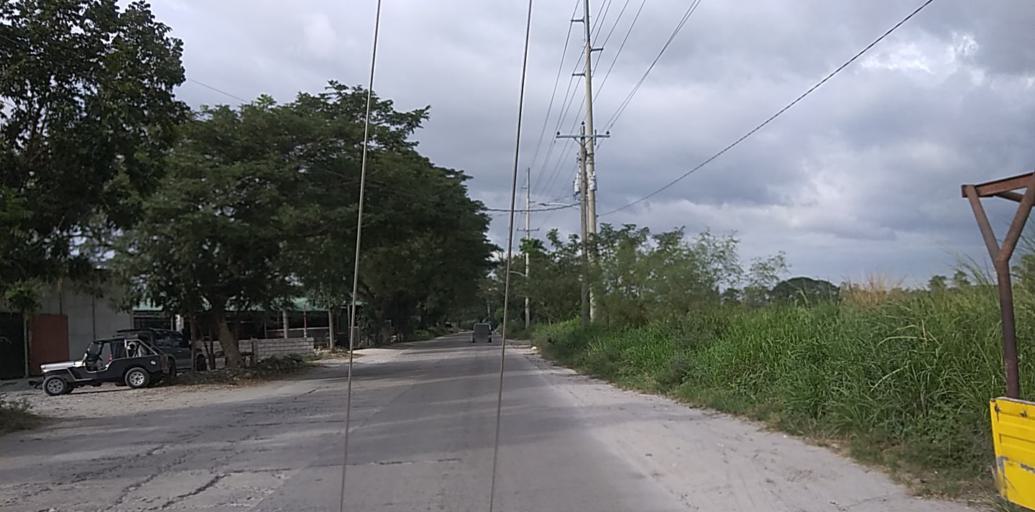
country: PH
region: Central Luzon
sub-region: Province of Pampanga
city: Porac
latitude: 15.0756
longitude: 120.5496
